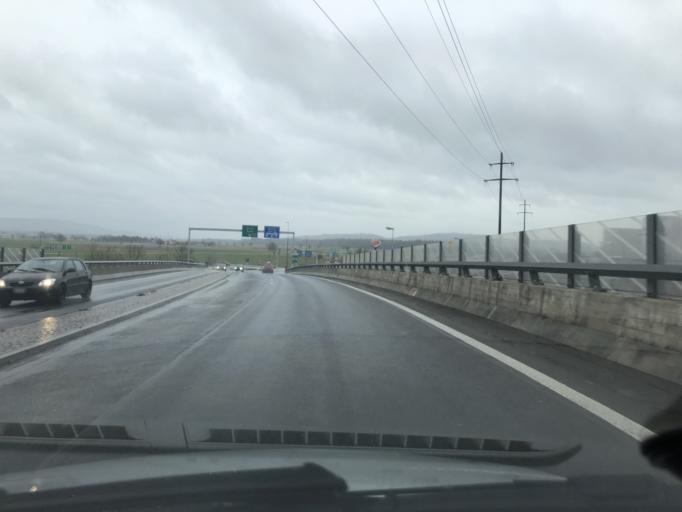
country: CH
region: Aargau
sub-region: Bezirk Brugg
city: Hausen
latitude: 47.4519
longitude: 8.2135
